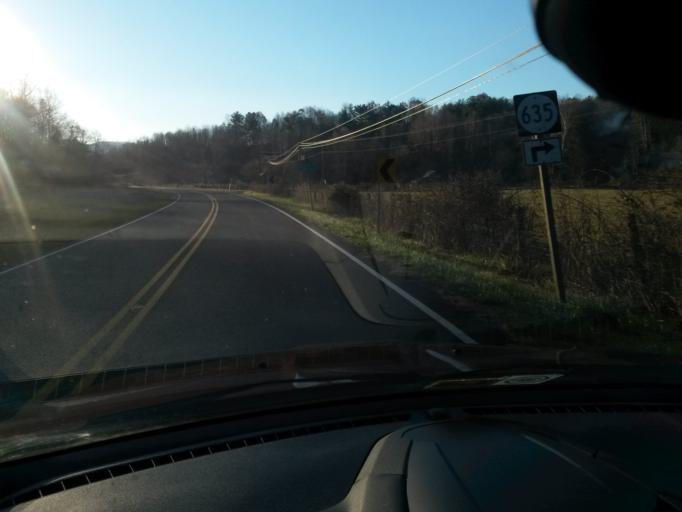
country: US
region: Virginia
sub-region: City of Buena Vista
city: Buena Vista
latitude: 37.6714
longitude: -79.2161
